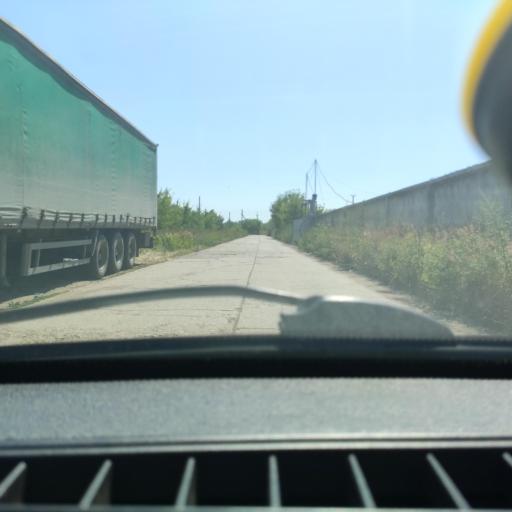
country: RU
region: Samara
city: Tol'yatti
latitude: 53.5702
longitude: 49.3612
